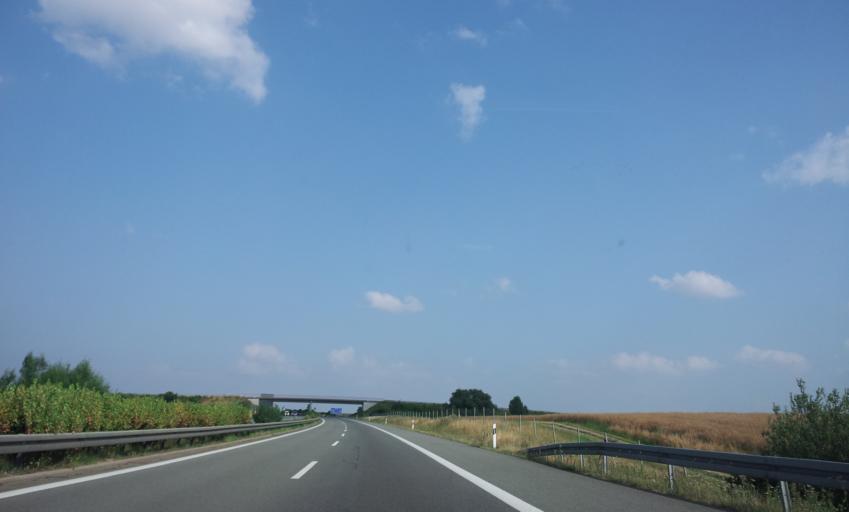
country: DE
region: Mecklenburg-Vorpommern
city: Neuenkirchen
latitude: 53.5795
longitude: 13.4263
